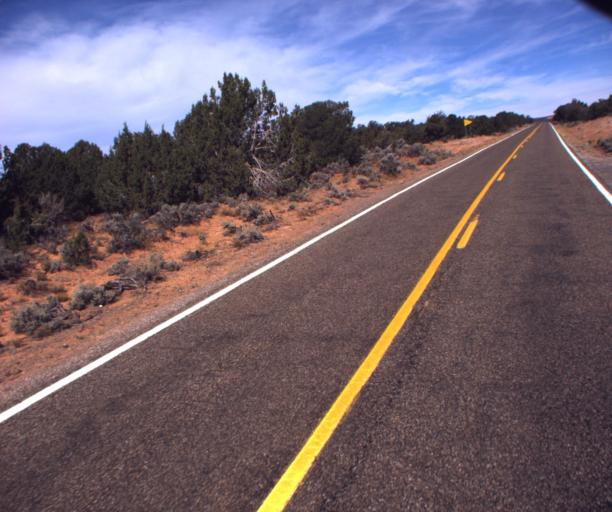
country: US
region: Arizona
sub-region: Navajo County
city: Kayenta
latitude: 36.5932
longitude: -110.4962
